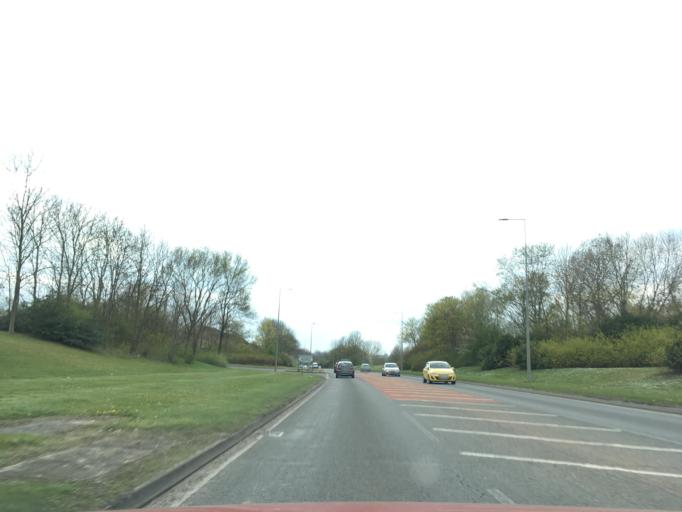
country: GB
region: England
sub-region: Milton Keynes
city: Milton Keynes
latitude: 52.0280
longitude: -0.7540
